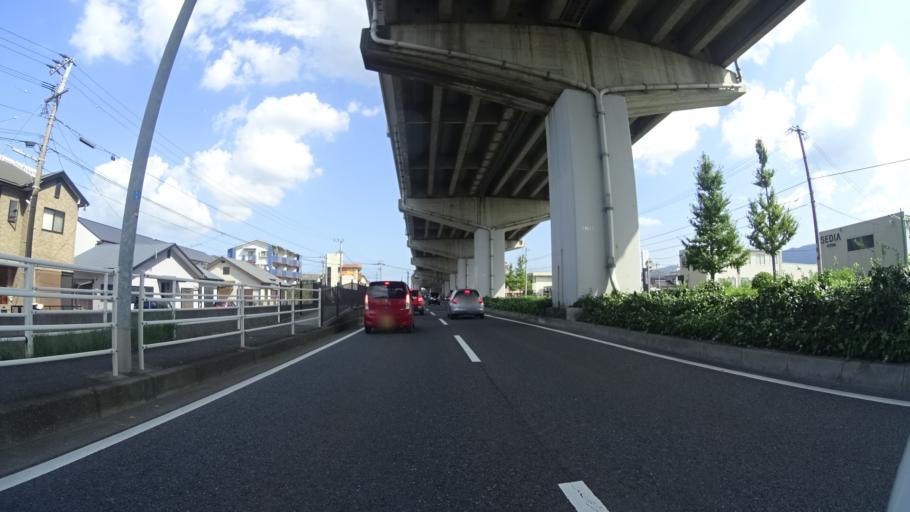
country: JP
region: Fukuoka
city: Kitakyushu
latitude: 33.8406
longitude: 130.8957
